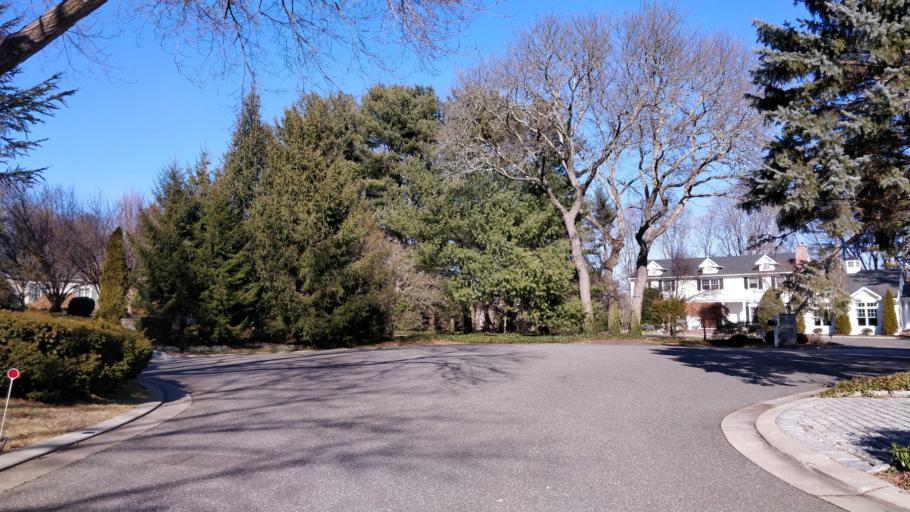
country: US
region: New York
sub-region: Nassau County
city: Old Brookville
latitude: 40.8251
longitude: -73.6114
